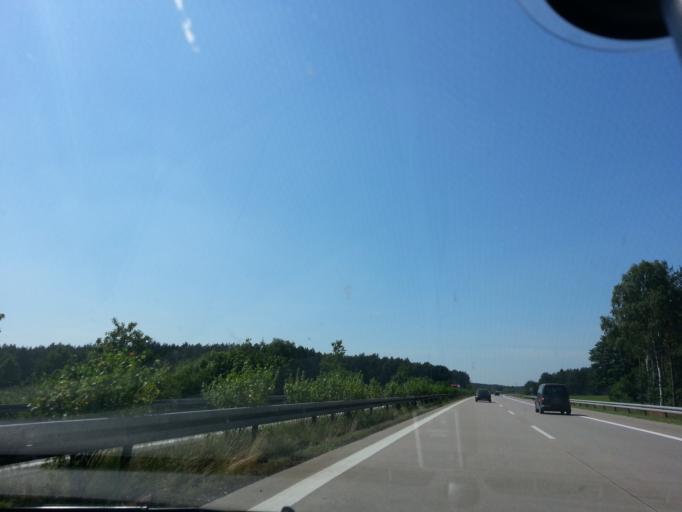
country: DE
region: Mecklenburg-Vorpommern
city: Rastow
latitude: 53.4322
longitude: 11.4090
